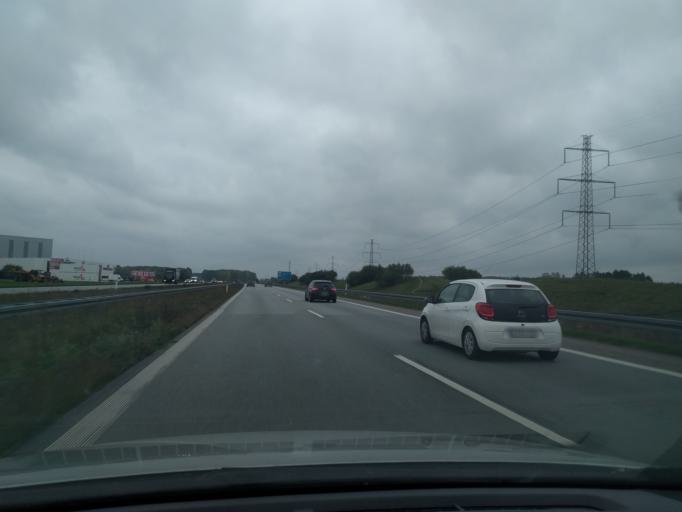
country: DK
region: Zealand
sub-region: Ringsted Kommune
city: Ringsted
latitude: 55.4563
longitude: 11.8060
